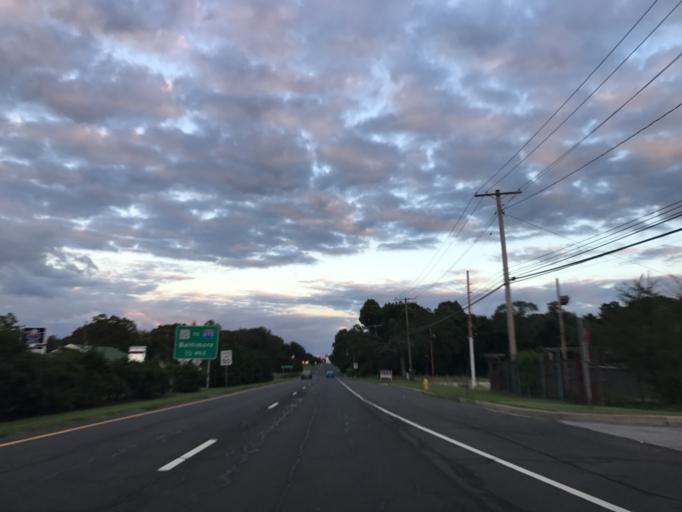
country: US
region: Maryland
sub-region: Anne Arundel County
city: Pasadena
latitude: 39.1211
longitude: -76.5854
